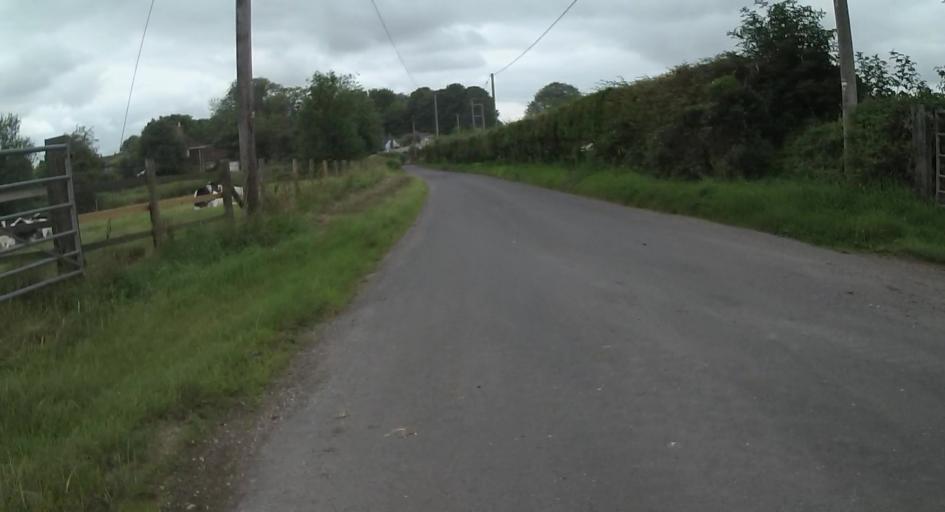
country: GB
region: England
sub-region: Hampshire
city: Four Marks
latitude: 51.0853
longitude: -1.1336
